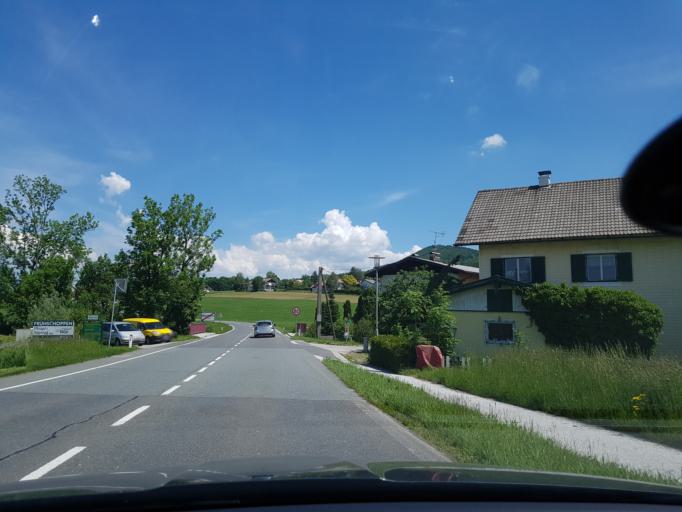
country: AT
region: Salzburg
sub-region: Politischer Bezirk Salzburg-Umgebung
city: Obertrum am See
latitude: 47.9392
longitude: 13.0866
